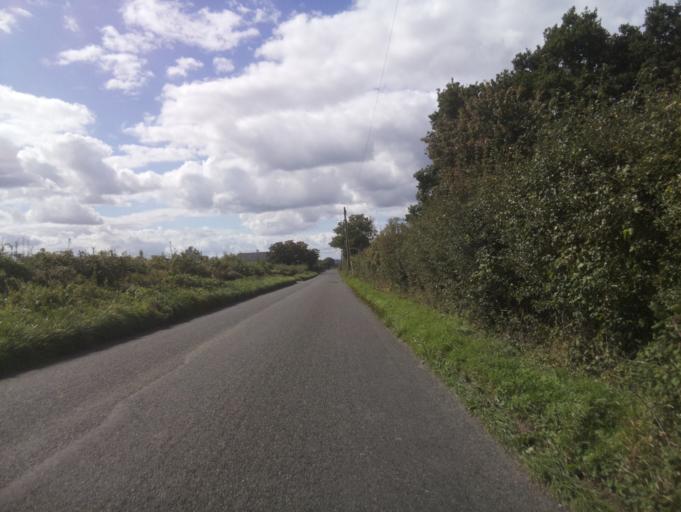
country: GB
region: England
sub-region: Wiltshire
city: Melksham
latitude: 51.3227
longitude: -2.1524
